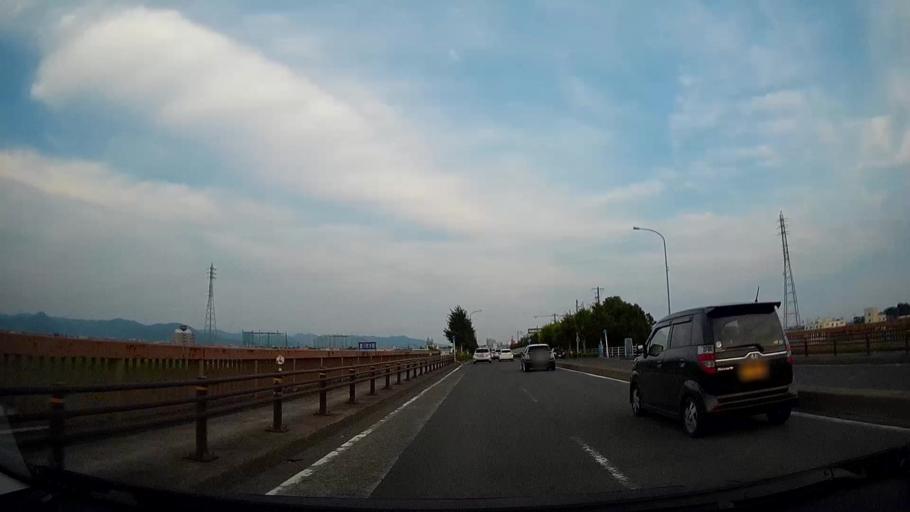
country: JP
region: Aichi
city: Kozakai-cho
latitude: 34.7928
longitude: 137.3712
